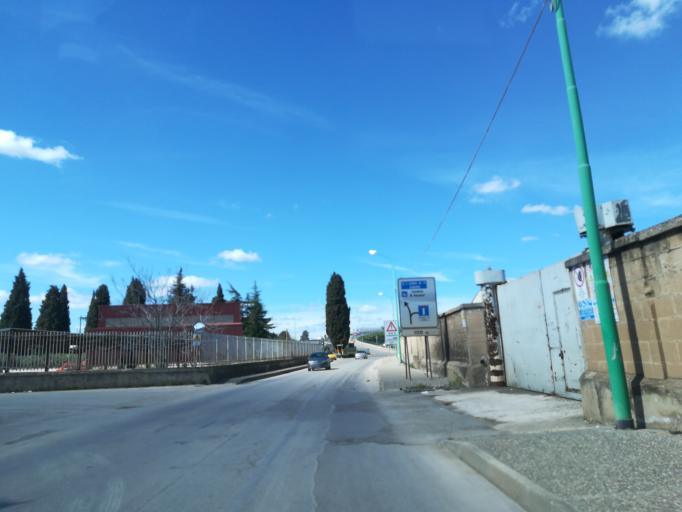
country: IT
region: Apulia
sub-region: Provincia di Bari
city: Terlizzi
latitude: 41.1244
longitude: 16.5448
